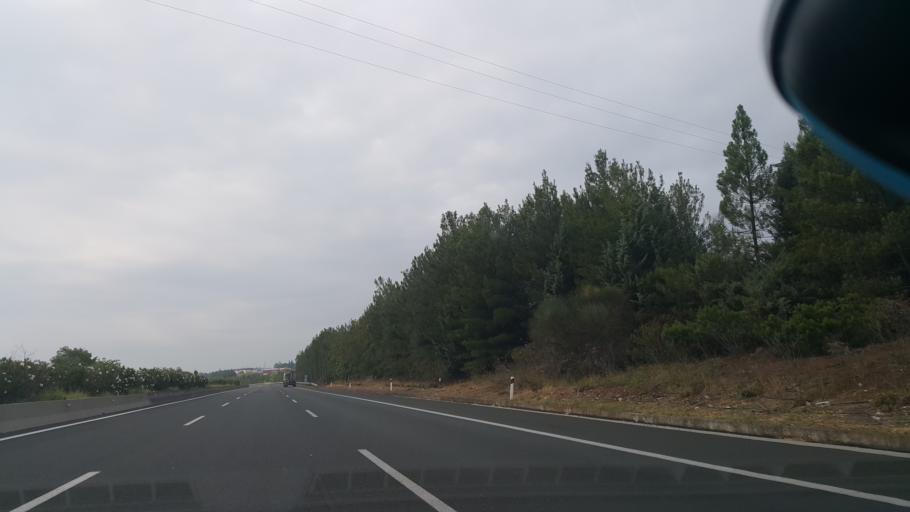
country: GR
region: Central Macedonia
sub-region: Nomos Pierias
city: Aiginio
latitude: 40.4768
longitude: 22.5702
